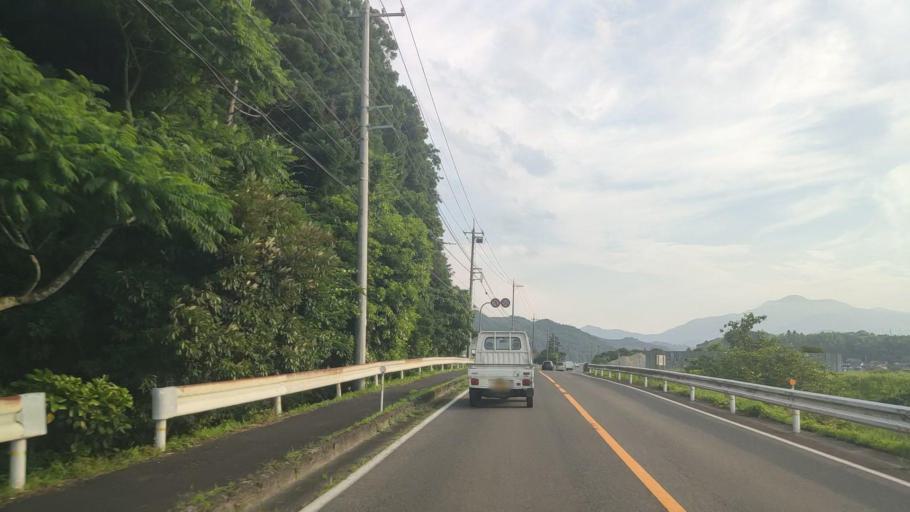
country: JP
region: Tottori
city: Kurayoshi
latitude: 35.3826
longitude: 133.7779
